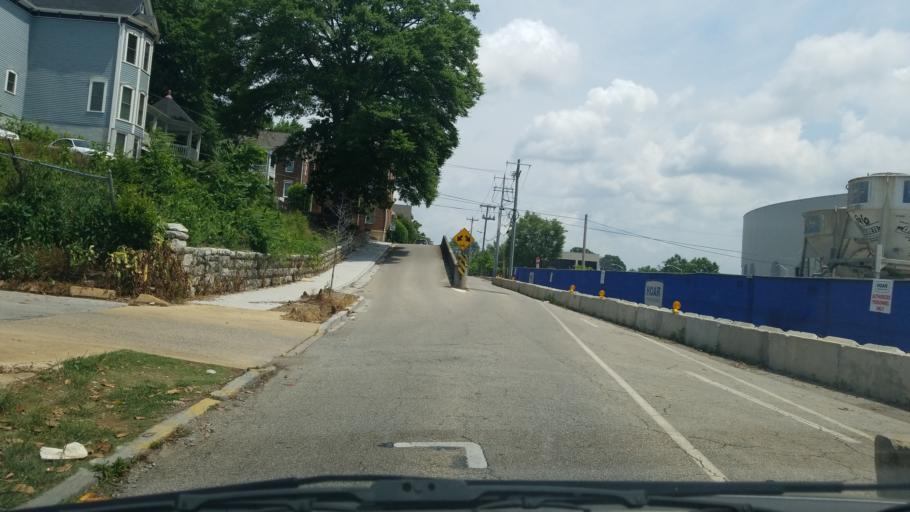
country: US
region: Tennessee
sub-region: Hamilton County
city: Chattanooga
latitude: 35.0496
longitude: -85.3027
